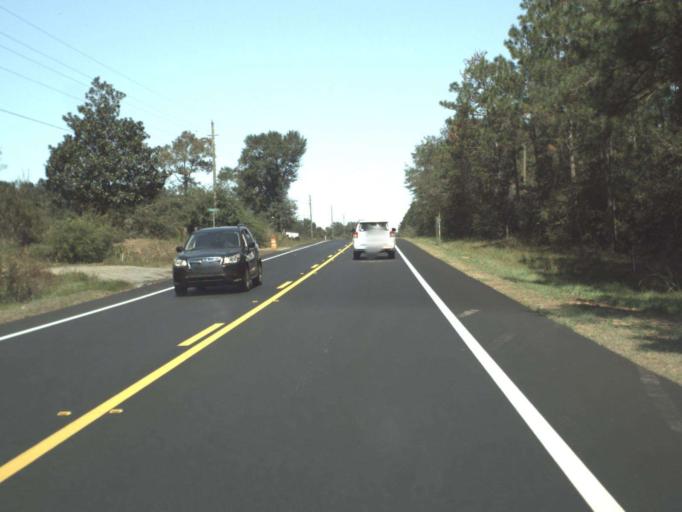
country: US
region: Alabama
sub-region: Covington County
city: Florala
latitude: 30.9111
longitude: -86.2812
